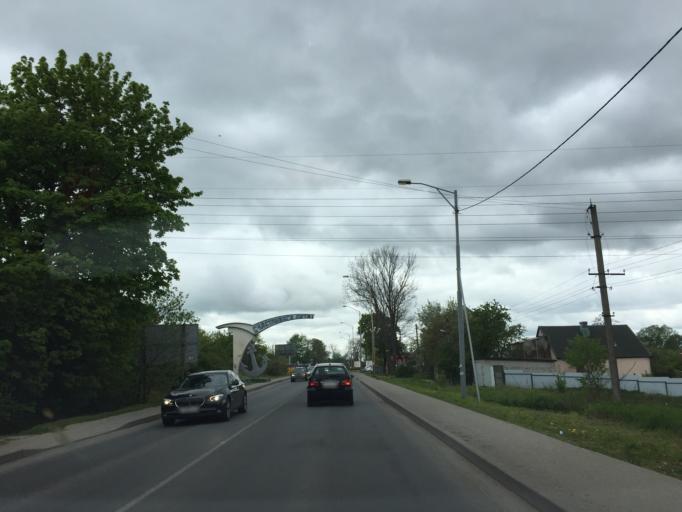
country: RU
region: Kaliningrad
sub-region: Gorod Kaliningrad
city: Kaliningrad
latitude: 54.6706
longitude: 20.4319
